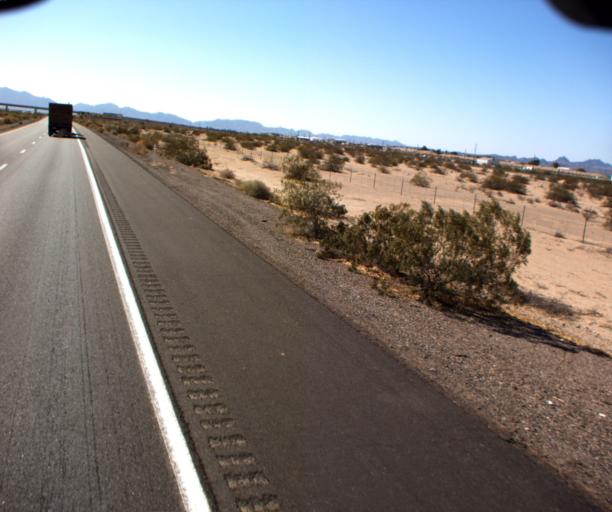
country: US
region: Arizona
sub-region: Yuma County
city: Wellton
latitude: 32.6716
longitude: -114.1016
